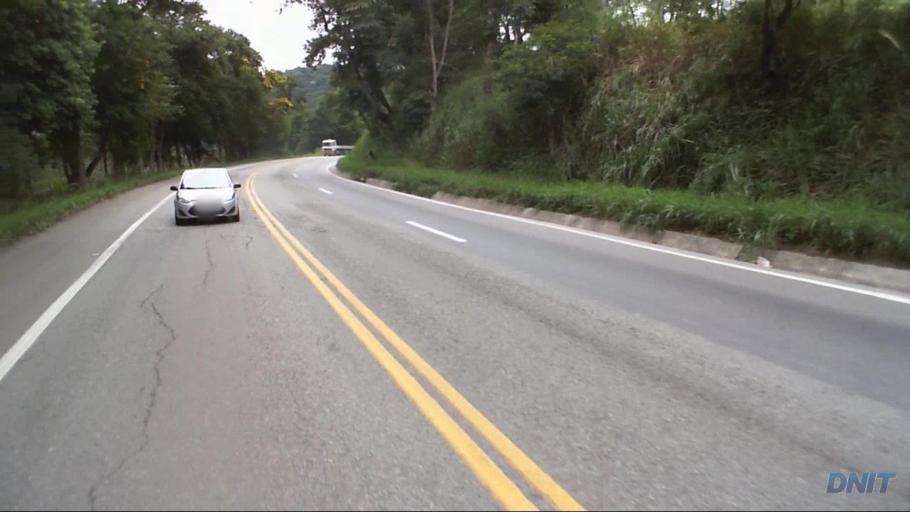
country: BR
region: Minas Gerais
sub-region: Nova Era
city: Nova Era
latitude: -19.7108
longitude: -43.0005
